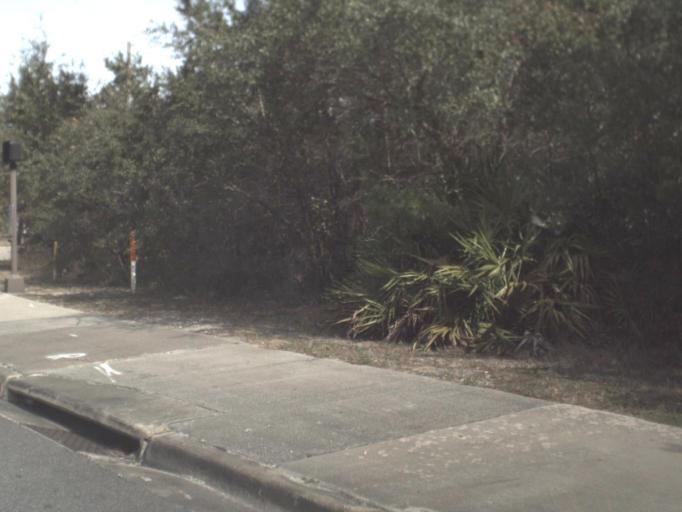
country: US
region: Florida
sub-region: Bay County
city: Pretty Bayou
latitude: 30.1879
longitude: -85.7200
